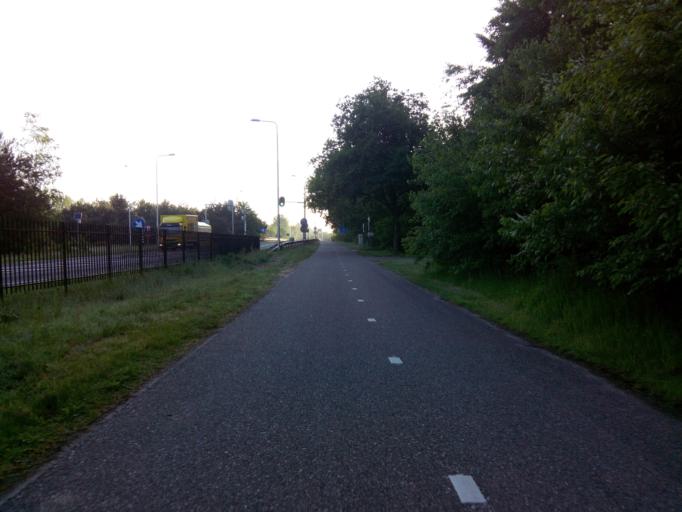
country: NL
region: Utrecht
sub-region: Gemeente Amersfoort
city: Amersfoort
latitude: 52.1270
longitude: 5.3659
